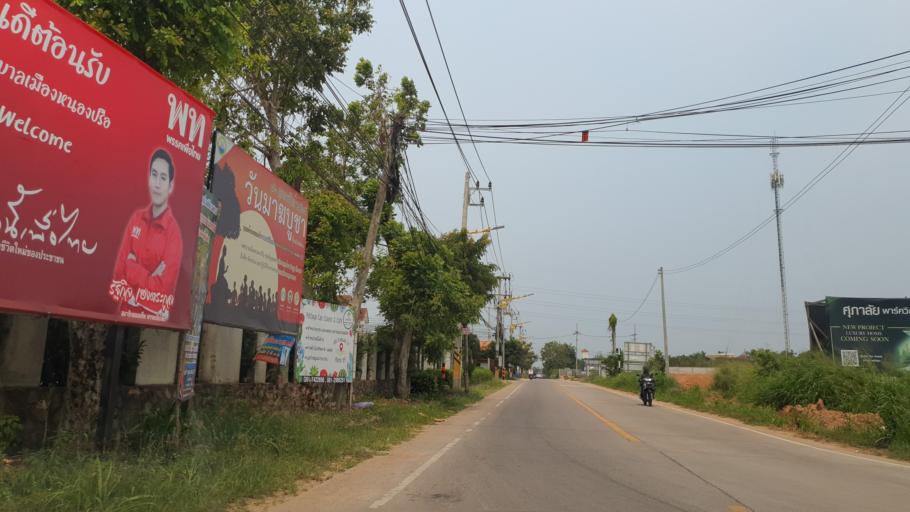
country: TH
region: Chon Buri
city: Phatthaya
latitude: 12.8956
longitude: 100.9207
